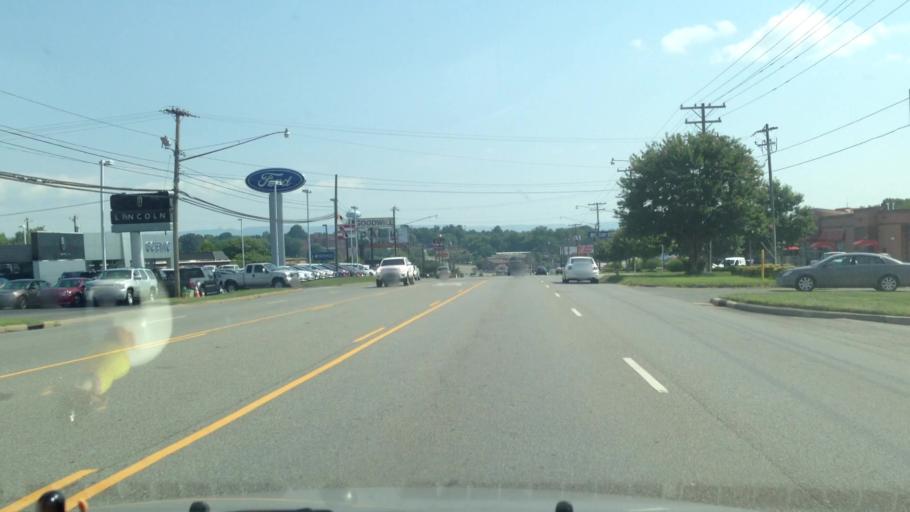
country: US
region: North Carolina
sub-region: Surry County
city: Mount Airy
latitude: 36.4804
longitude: -80.6156
